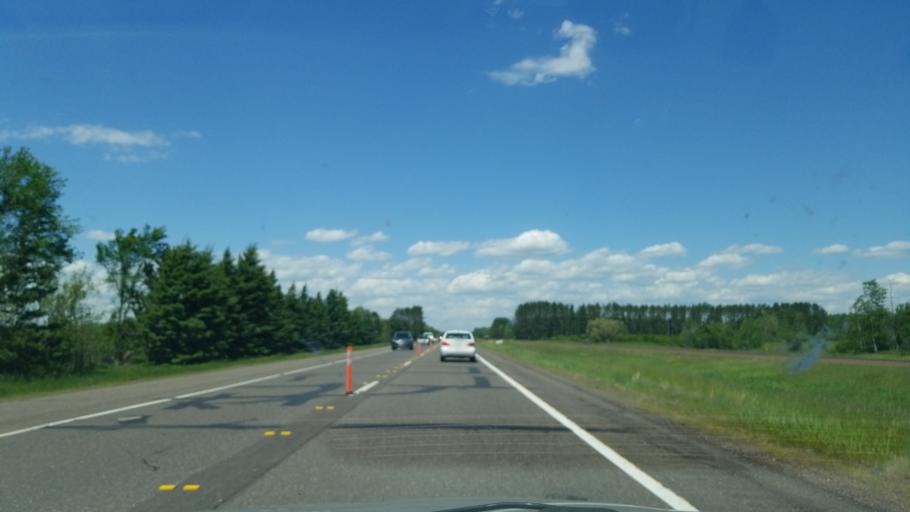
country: US
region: Minnesota
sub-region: Pine County
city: Sandstone
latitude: 46.2756
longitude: -92.8244
